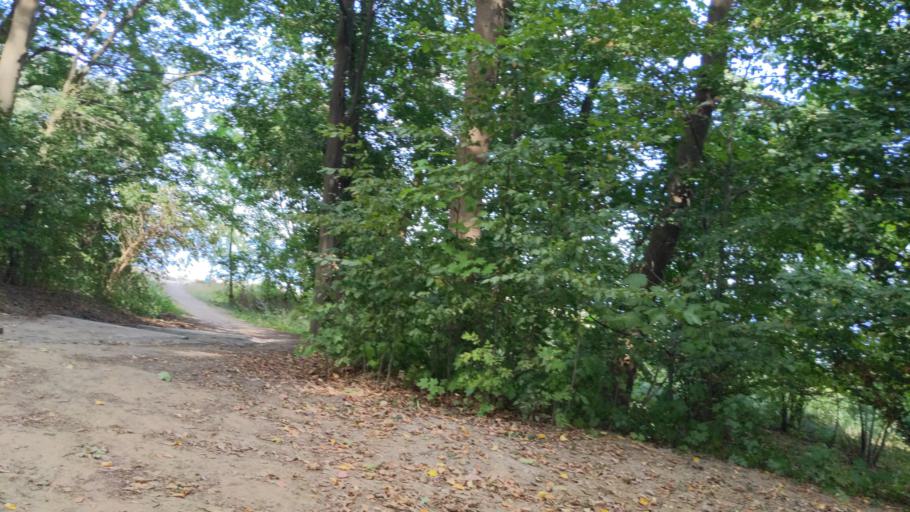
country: DE
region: Mecklenburg-Vorpommern
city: Wismar
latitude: 53.9105
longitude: 11.4318
